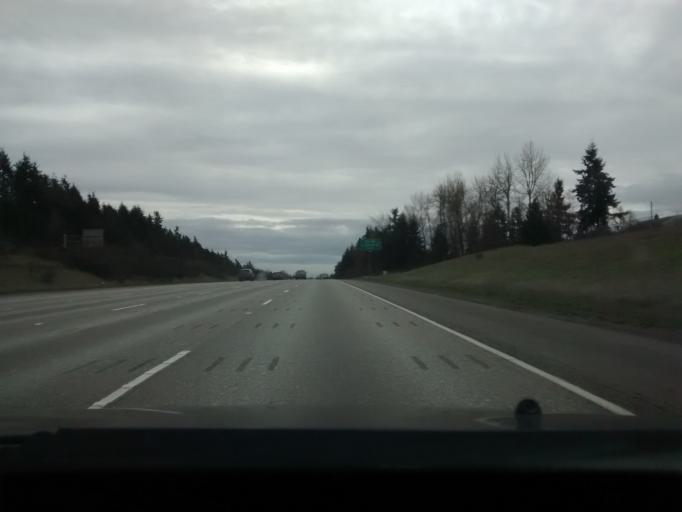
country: US
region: Washington
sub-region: King County
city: Des Moines
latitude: 47.3770
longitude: -122.2920
